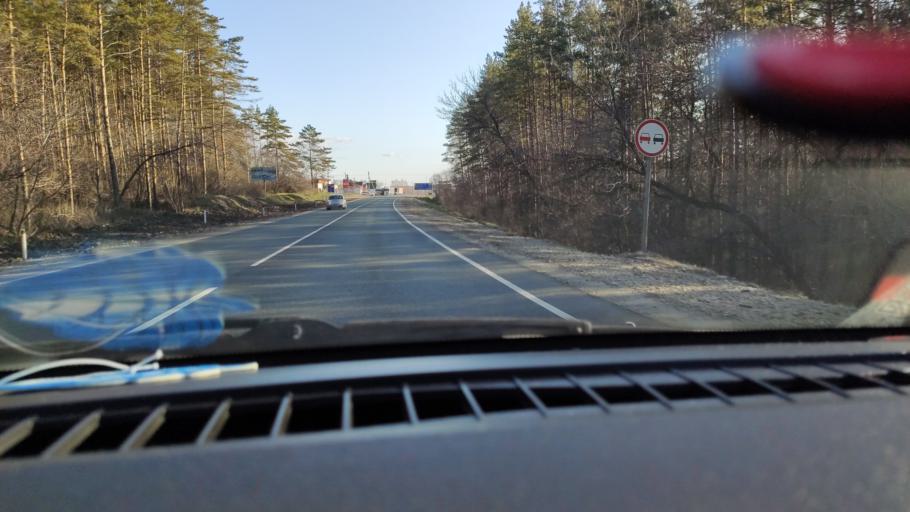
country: RU
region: Saratov
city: Khvalynsk
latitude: 52.5220
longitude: 48.0200
